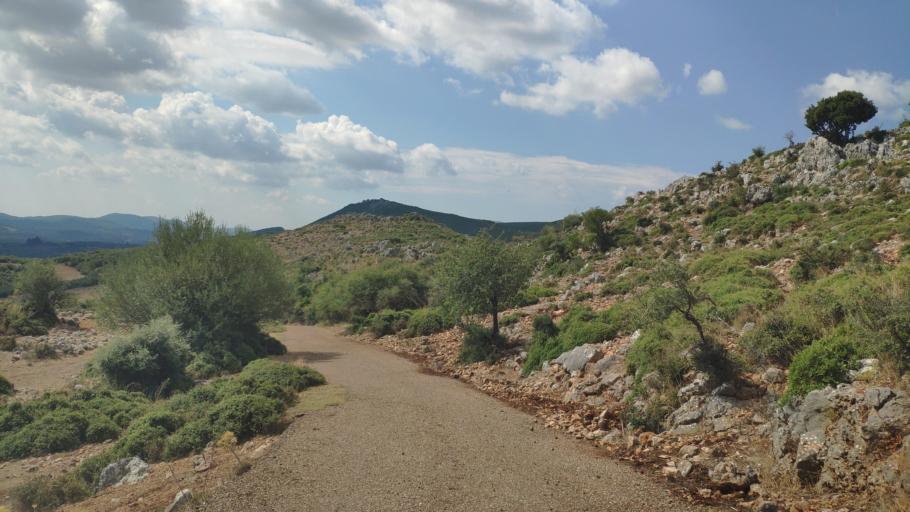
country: GR
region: West Greece
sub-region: Nomos Aitolias kai Akarnanias
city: Fitiai
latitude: 38.6813
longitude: 21.1402
